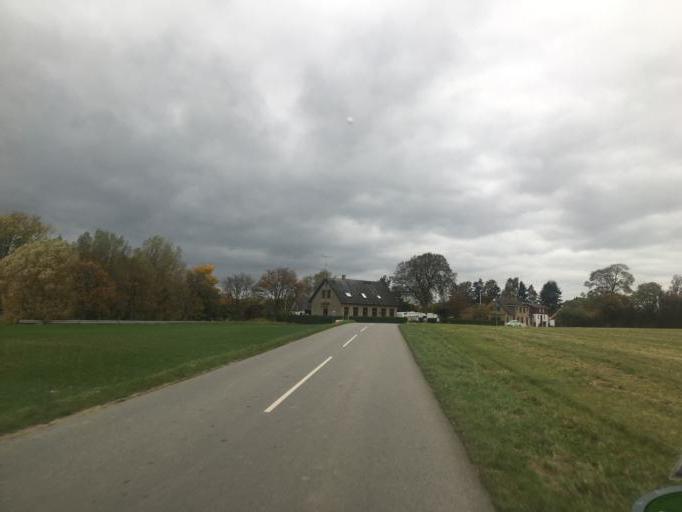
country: DK
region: Zealand
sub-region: Koge Kommune
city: Bjaeverskov
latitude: 55.4235
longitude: 11.9817
